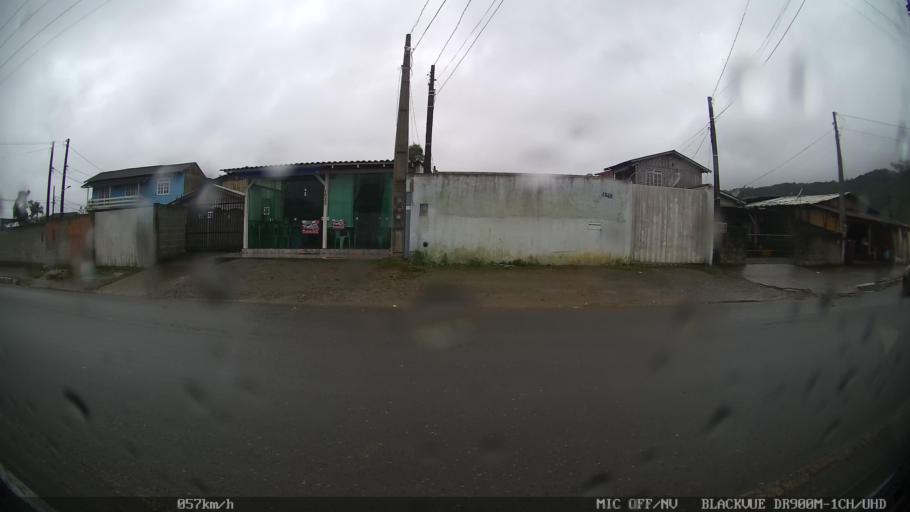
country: BR
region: Santa Catarina
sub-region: Itajai
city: Itajai
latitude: -26.9311
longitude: -48.6912
